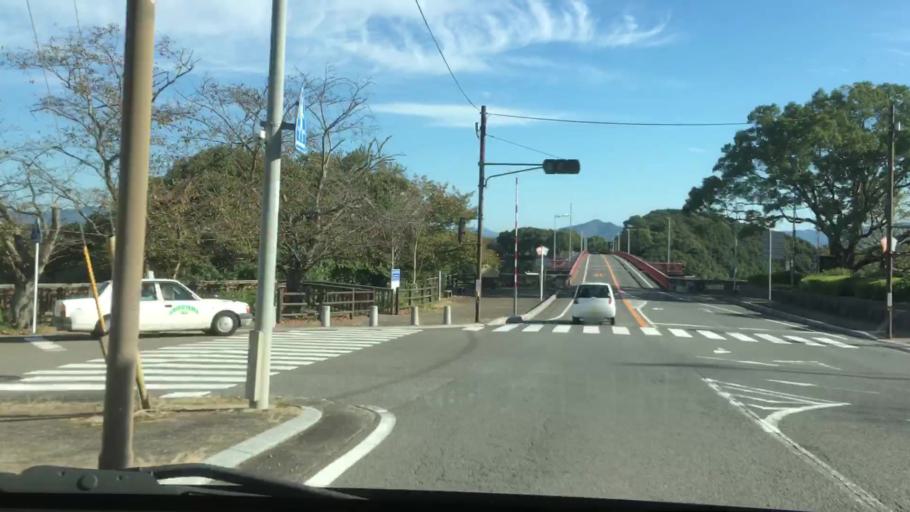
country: JP
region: Nagasaki
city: Sasebo
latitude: 33.0516
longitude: 129.7563
